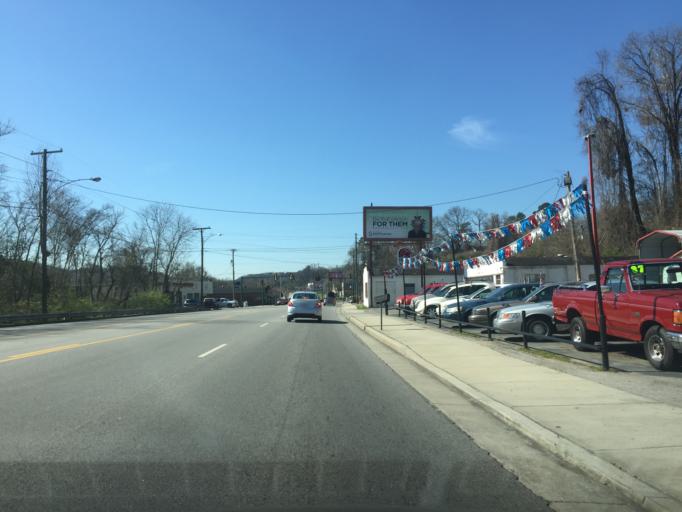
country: US
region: Tennessee
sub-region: Hamilton County
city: Red Bank
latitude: 35.0956
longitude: -85.3062
